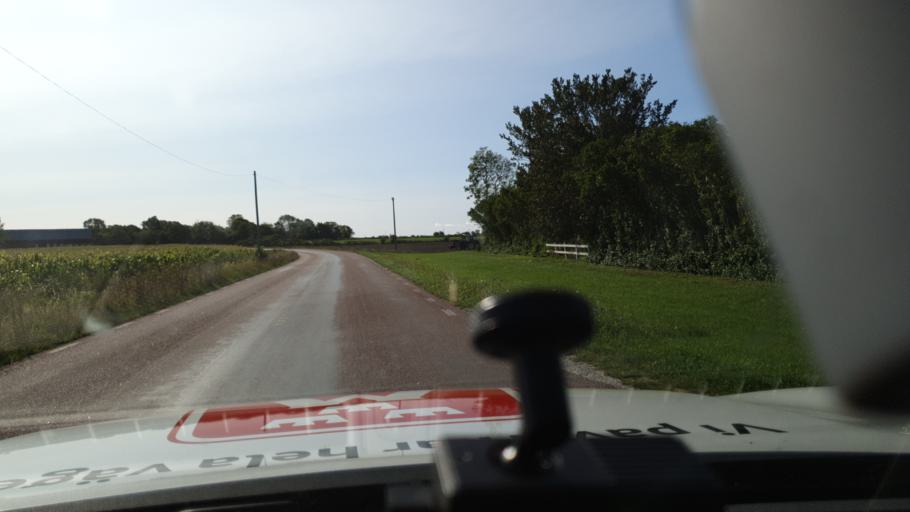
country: SE
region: Gotland
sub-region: Gotland
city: Hemse
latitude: 57.1544
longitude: 18.2814
